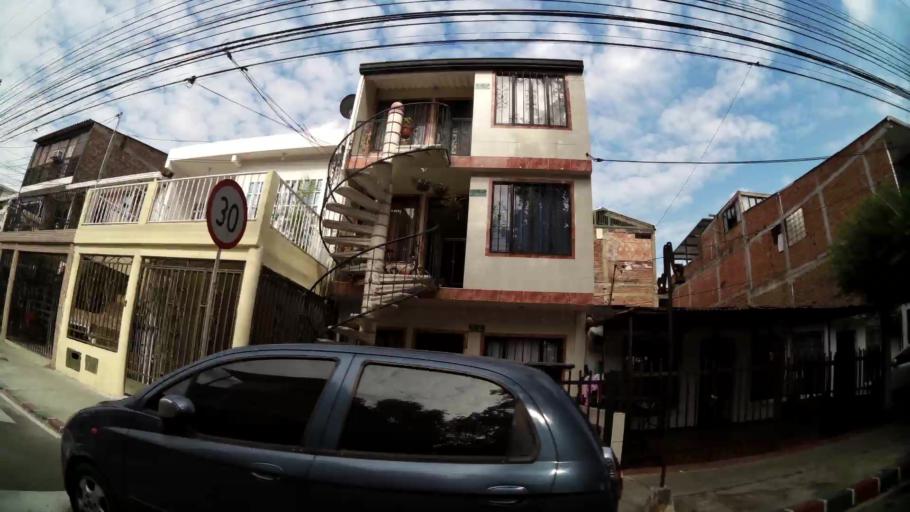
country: CO
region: Valle del Cauca
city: Cali
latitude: 3.4887
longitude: -76.4963
